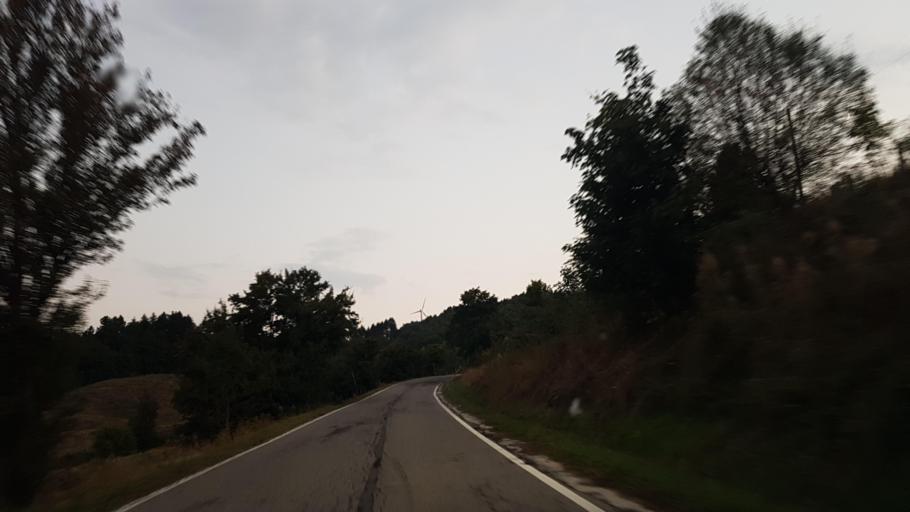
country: IT
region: Emilia-Romagna
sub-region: Provincia di Parma
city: Tornolo
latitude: 44.4313
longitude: 9.6238
